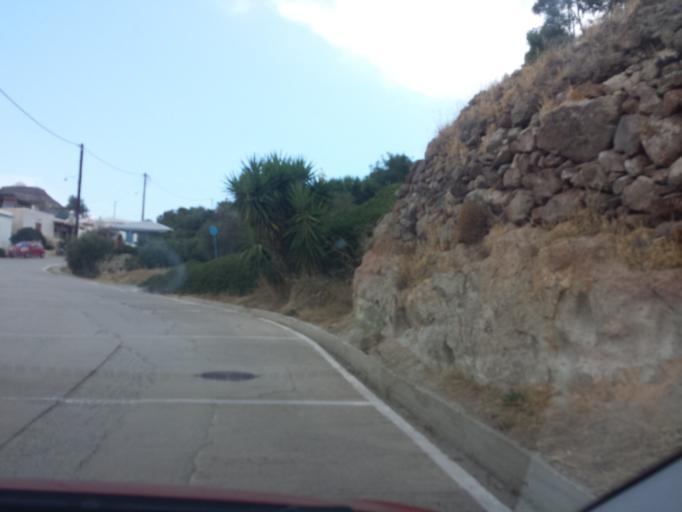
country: GR
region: South Aegean
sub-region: Nomos Kykladon
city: Milos
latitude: 36.7396
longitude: 24.4244
